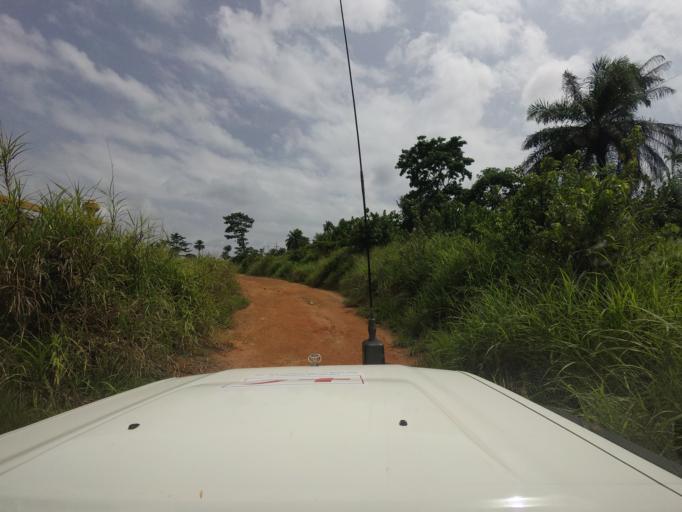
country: GN
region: Nzerekore
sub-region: Nzerekore Prefecture
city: Nzerekore
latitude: 7.7399
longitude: -8.7539
